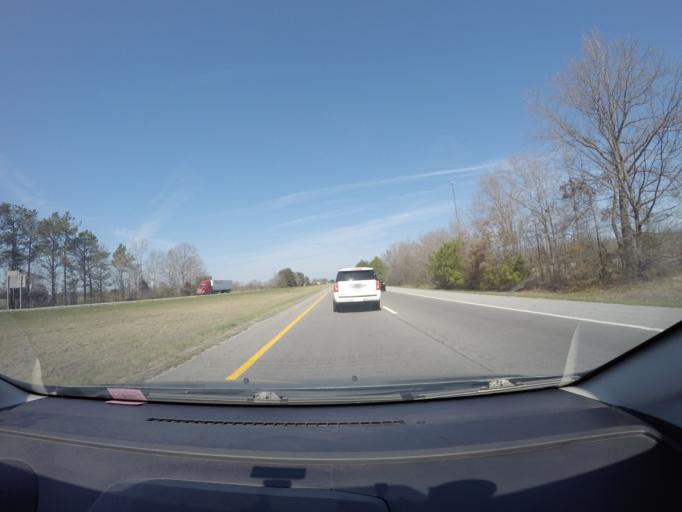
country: US
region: Tennessee
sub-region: Coffee County
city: New Union
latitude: 35.5134
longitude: -86.1139
